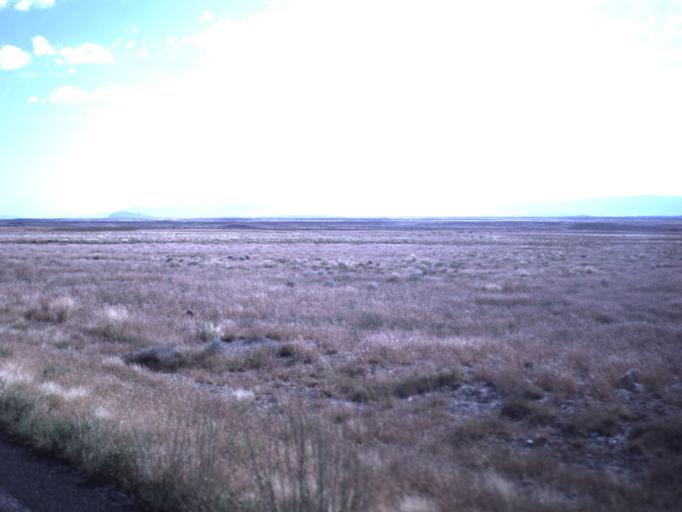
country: US
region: Utah
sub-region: Beaver County
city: Milford
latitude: 38.8554
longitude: -112.8406
